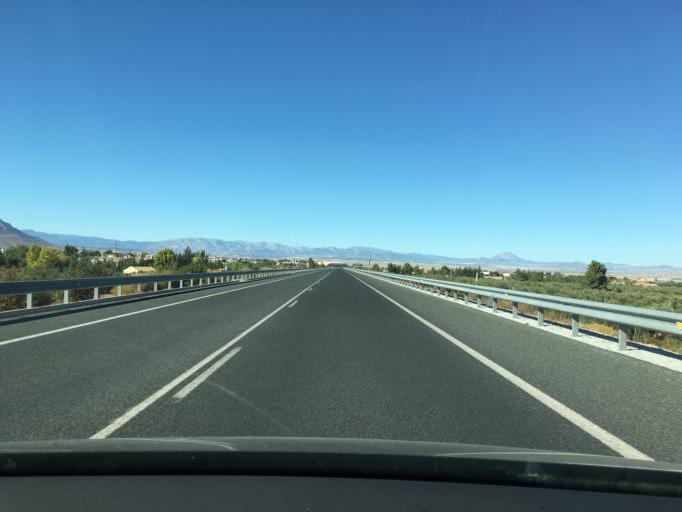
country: ES
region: Andalusia
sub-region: Provincia de Granada
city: Baza
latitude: 37.4934
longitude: -2.7398
